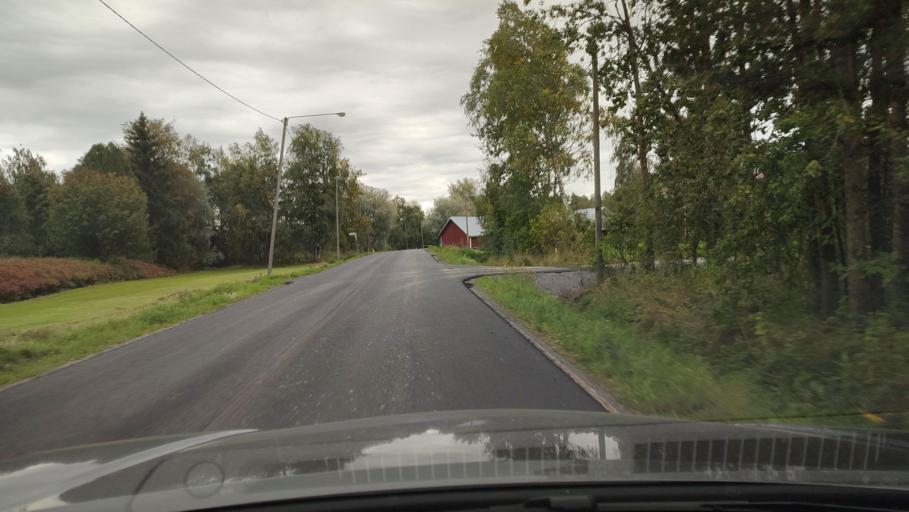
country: FI
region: Ostrobothnia
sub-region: Sydosterbotten
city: Kristinestad
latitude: 62.2500
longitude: 21.5243
